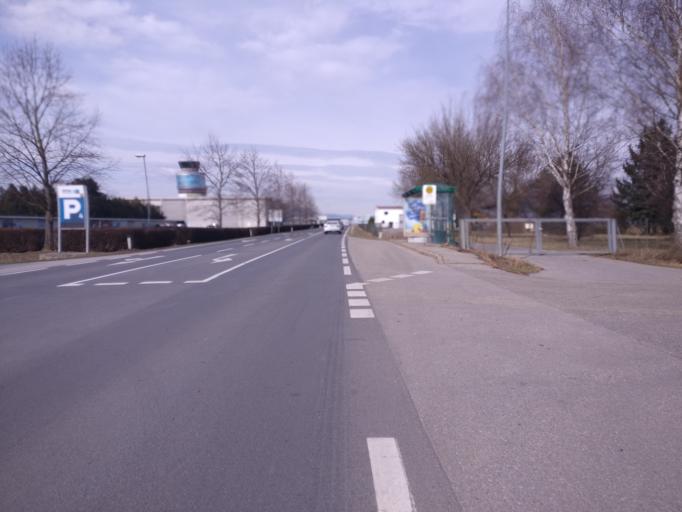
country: AT
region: Styria
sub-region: Politischer Bezirk Graz-Umgebung
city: Feldkirchen bei Graz
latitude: 46.9933
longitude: 15.4484
